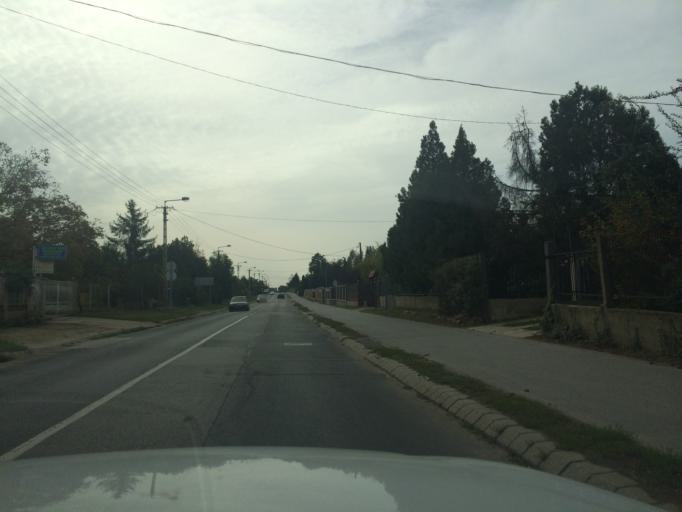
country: HU
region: Szabolcs-Szatmar-Bereg
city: Nyiregyhaza
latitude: 47.9940
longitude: 21.7306
